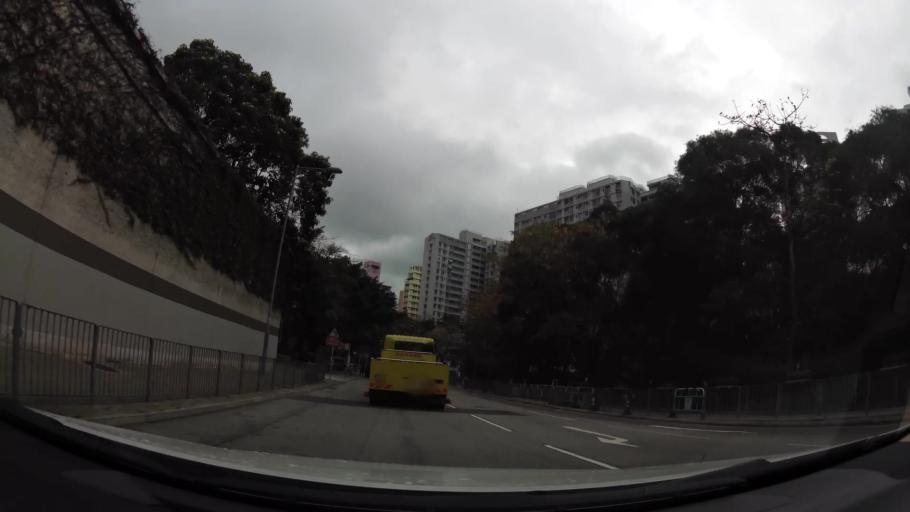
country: HK
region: Tsuen Wan
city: Tsuen Wan
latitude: 22.3661
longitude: 114.1309
